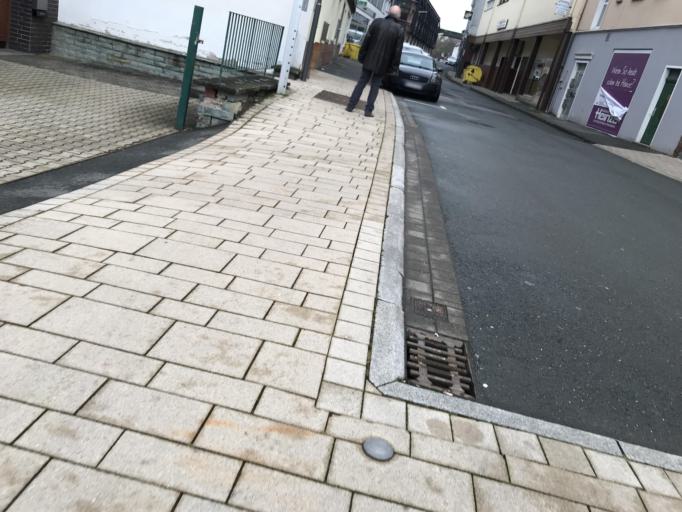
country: DE
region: Hesse
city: Frankenberg
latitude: 51.0597
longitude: 8.7966
